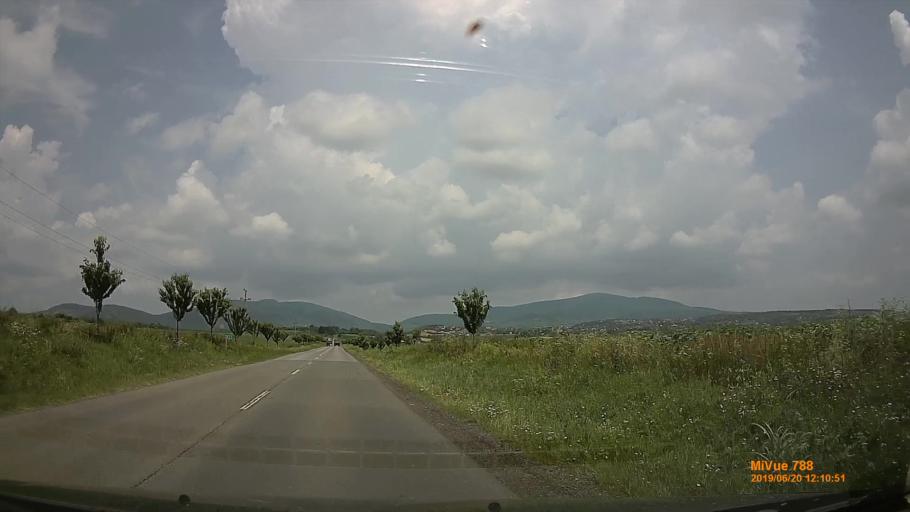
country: HU
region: Baranya
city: Hosszuheteny
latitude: 46.1287
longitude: 18.3485
